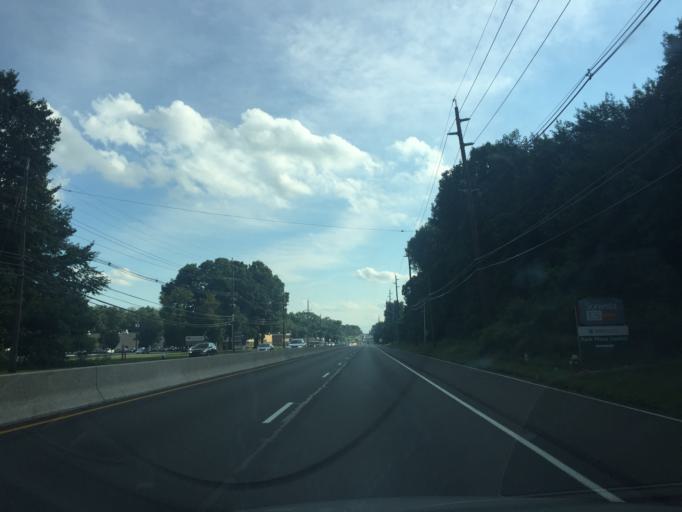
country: US
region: New Jersey
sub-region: Middlesex County
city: Heathcote
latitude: 40.3779
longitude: -74.5817
